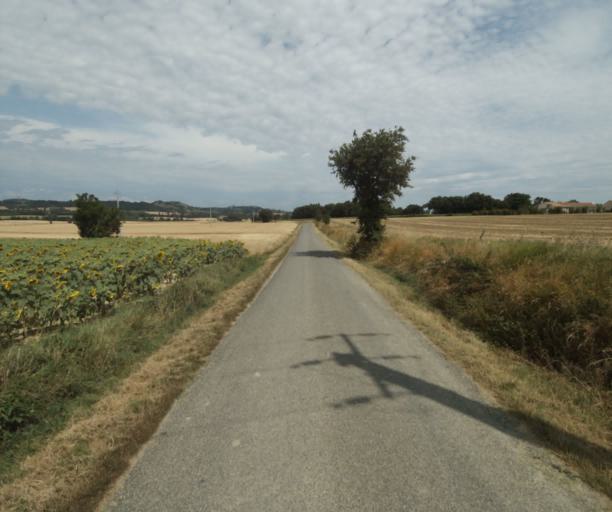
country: FR
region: Midi-Pyrenees
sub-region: Departement de la Haute-Garonne
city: Saint-Felix-Lauragais
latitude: 43.4124
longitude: 1.9041
